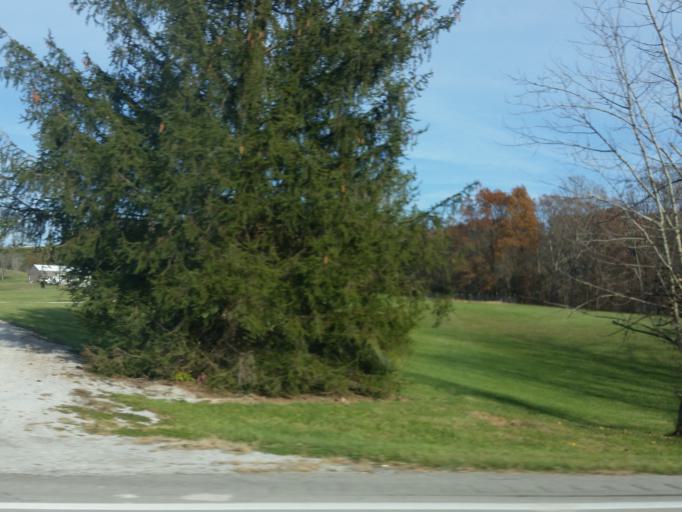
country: US
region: Kentucky
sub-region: Campbell County
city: Claryville
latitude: 38.8450
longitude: -84.3762
